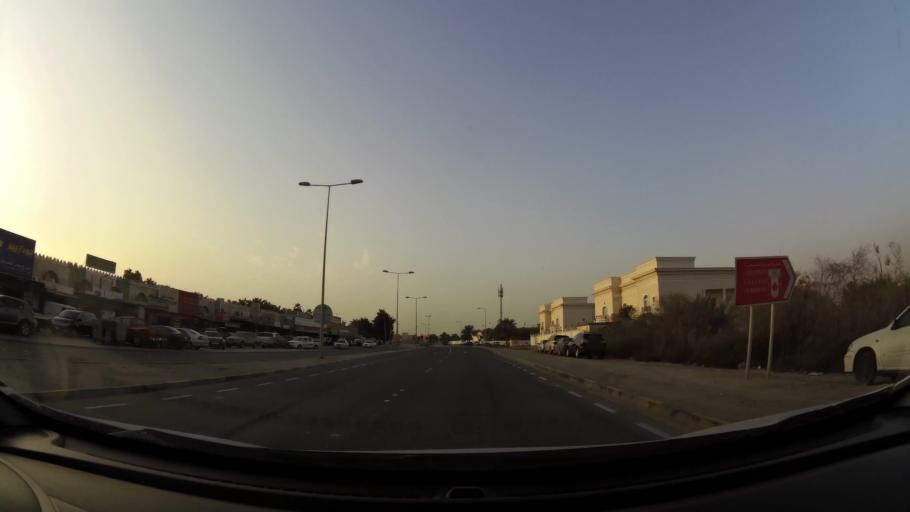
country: BH
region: Northern
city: Madinat `Isa
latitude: 26.1902
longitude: 50.4655
